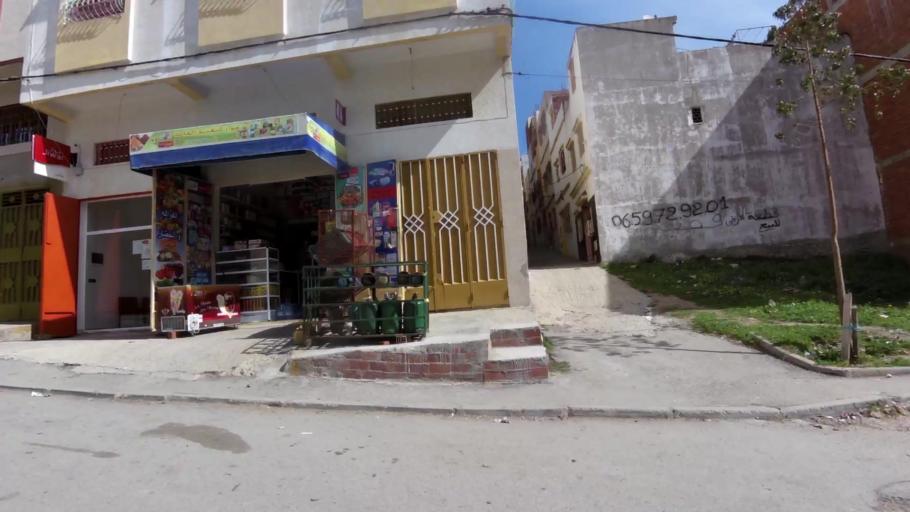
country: MA
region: Tanger-Tetouan
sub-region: Tanger-Assilah
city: Tangier
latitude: 35.7263
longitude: -5.8050
